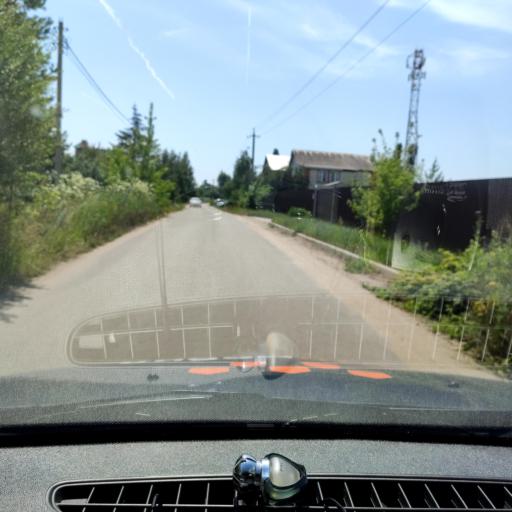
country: RU
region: Voronezj
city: Ramon'
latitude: 51.8309
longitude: 39.2657
